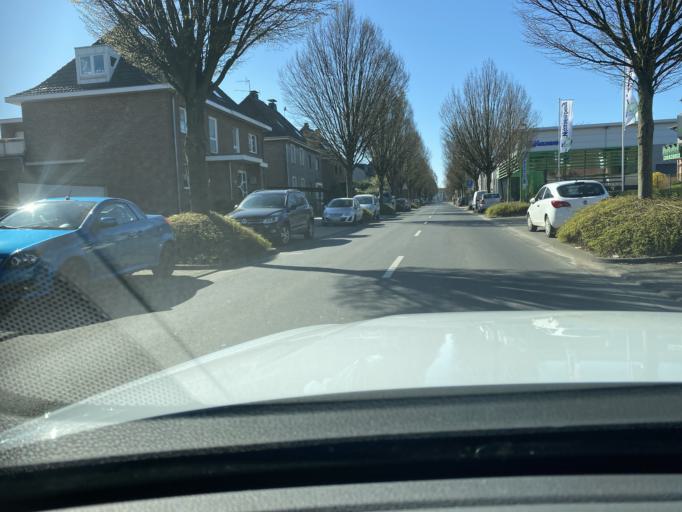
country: DE
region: North Rhine-Westphalia
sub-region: Regierungsbezirk Dusseldorf
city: Grevenbroich
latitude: 51.0966
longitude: 6.5828
